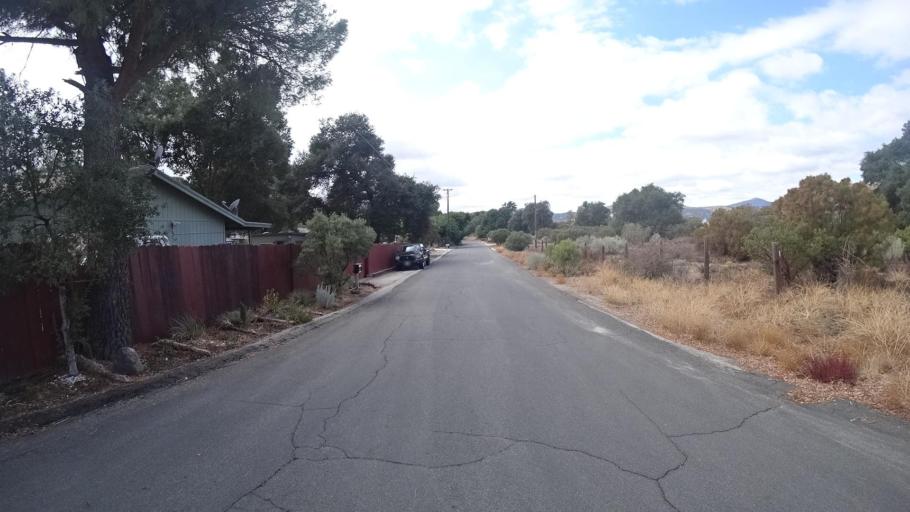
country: US
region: California
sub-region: San Diego County
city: Campo
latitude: 32.6865
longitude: -116.5130
